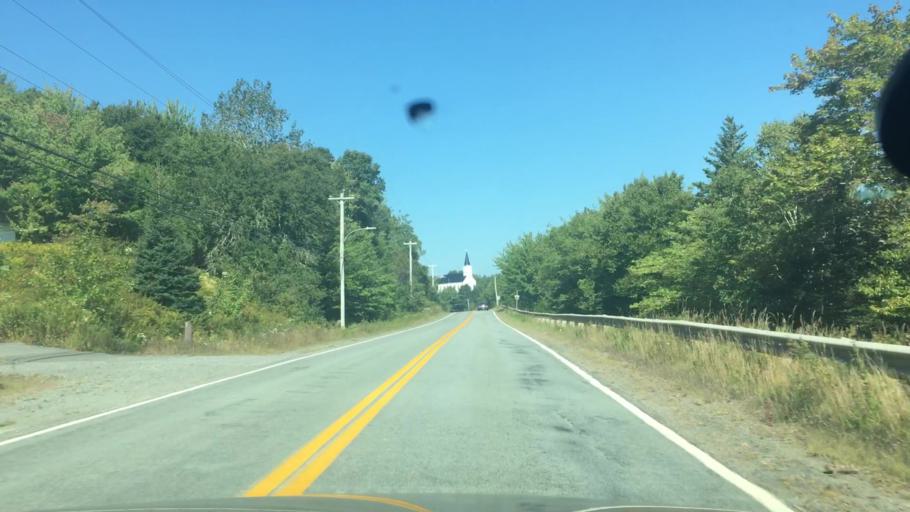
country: CA
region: Nova Scotia
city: New Glasgow
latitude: 44.9197
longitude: -62.5433
